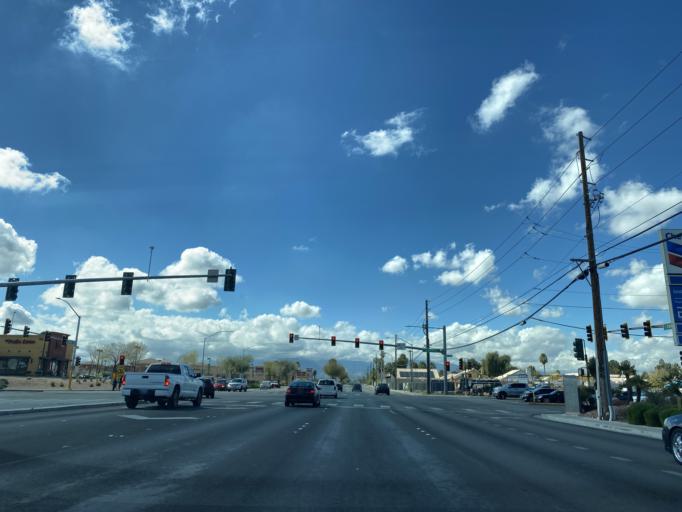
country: US
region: Nevada
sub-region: Clark County
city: North Las Vegas
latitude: 36.2395
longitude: -115.1795
